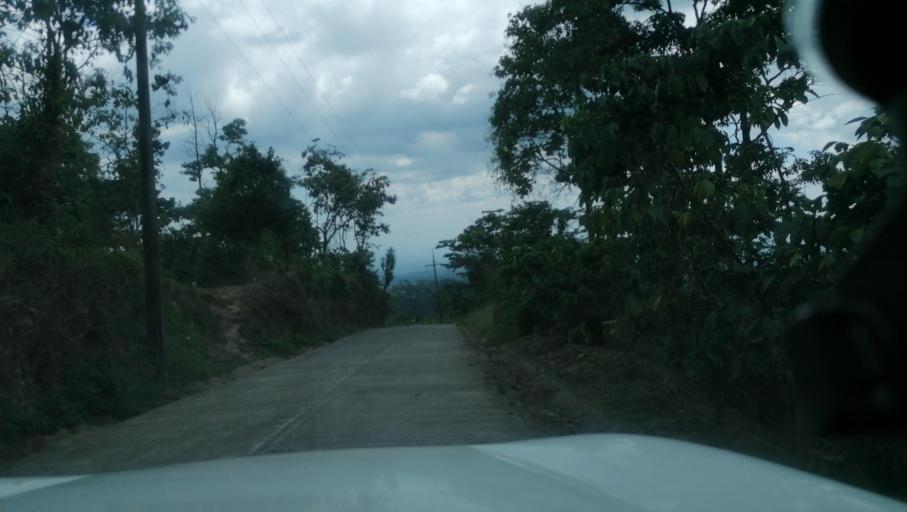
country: MX
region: Chiapas
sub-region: Cacahoatan
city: Benito Juarez
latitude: 15.0681
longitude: -92.1518
